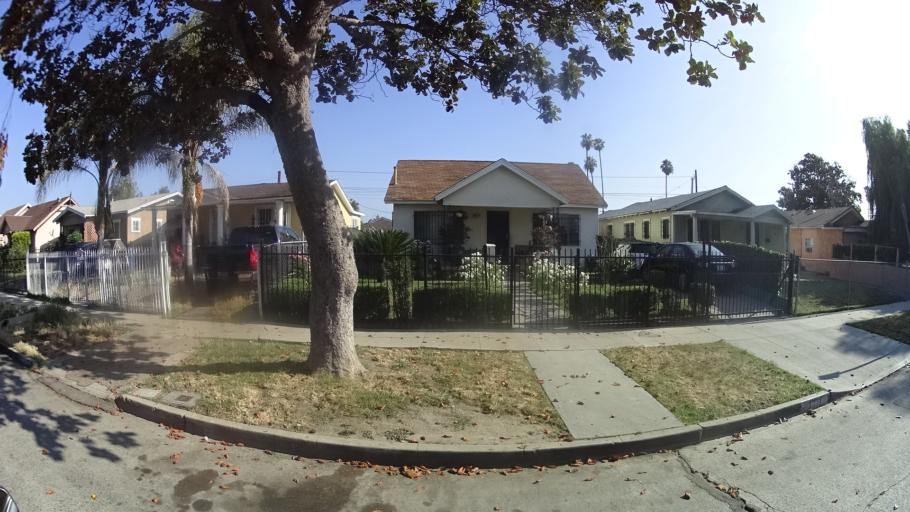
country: US
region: California
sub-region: Los Angeles County
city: Westmont
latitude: 33.9754
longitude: -118.2985
